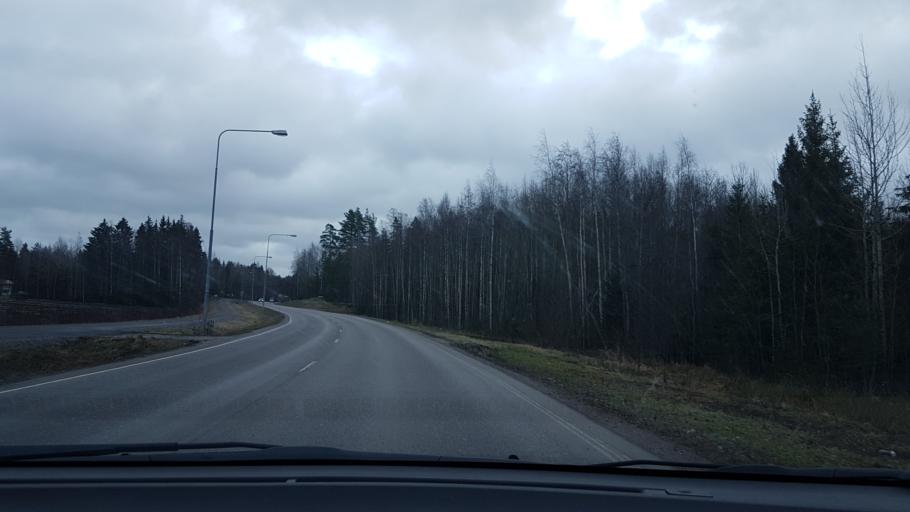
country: FI
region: Uusimaa
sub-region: Helsinki
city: Tuusula
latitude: 60.3717
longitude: 25.0648
